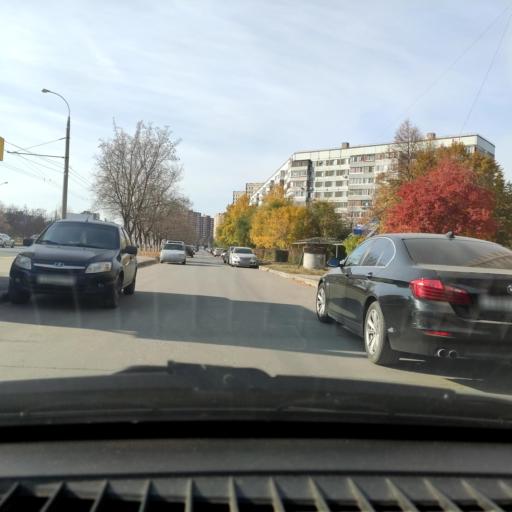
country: RU
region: Samara
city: Tol'yatti
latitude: 53.5211
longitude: 49.3177
